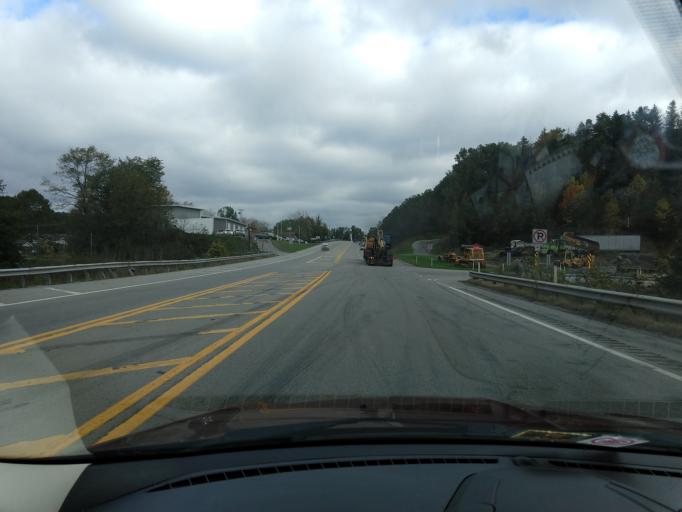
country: US
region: West Virginia
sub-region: Randolph County
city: Elkins
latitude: 38.8491
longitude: -79.8679
